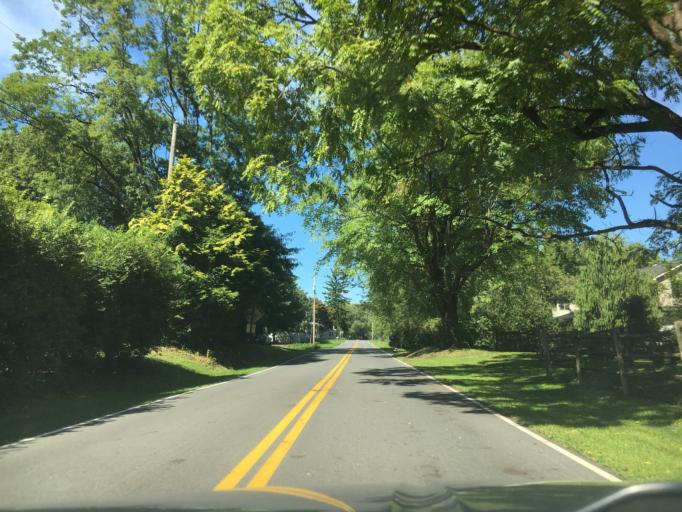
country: US
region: Pennsylvania
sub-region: Berks County
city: Topton
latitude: 40.5170
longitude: -75.6897
